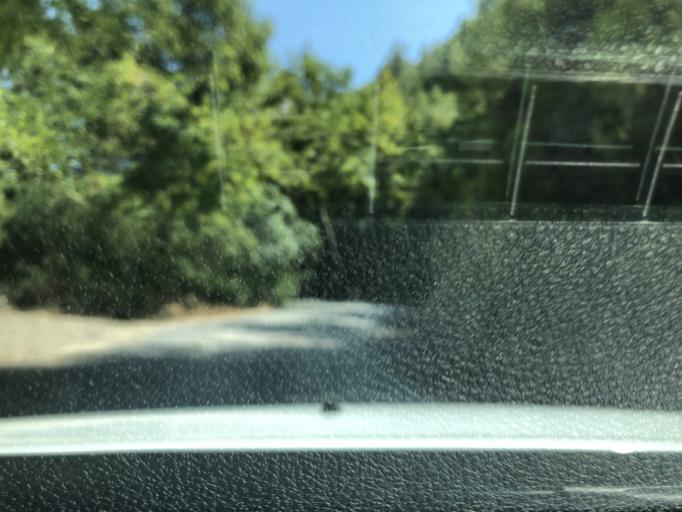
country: TR
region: Antalya
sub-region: Manavgat
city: Manavgat
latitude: 36.9053
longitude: 31.5601
